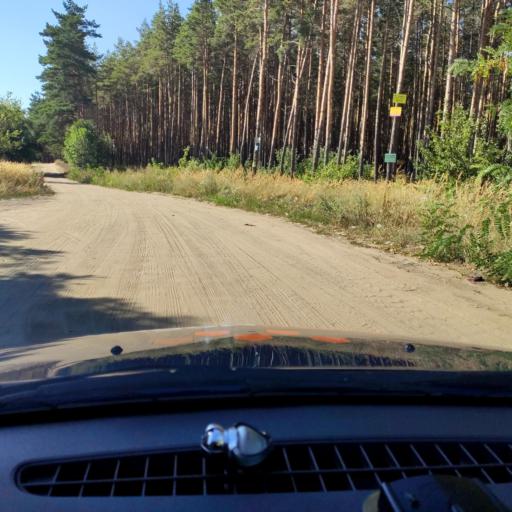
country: RU
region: Voronezj
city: Maslovka
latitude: 51.5312
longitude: 39.1658
